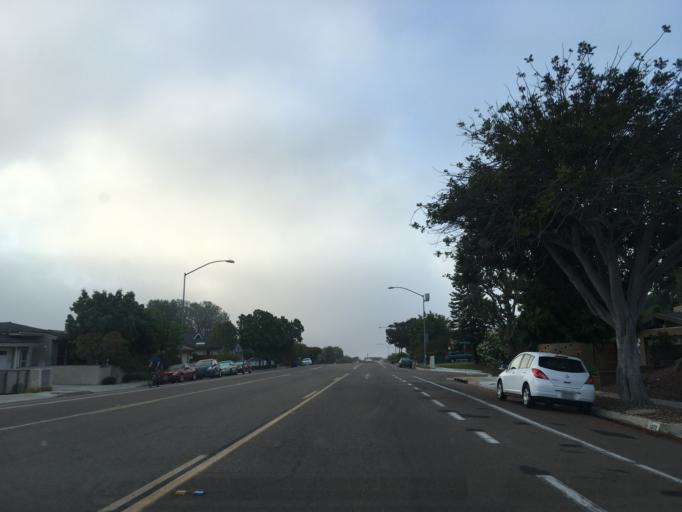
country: US
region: California
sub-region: San Diego County
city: La Jolla
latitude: 32.8240
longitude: -117.2360
